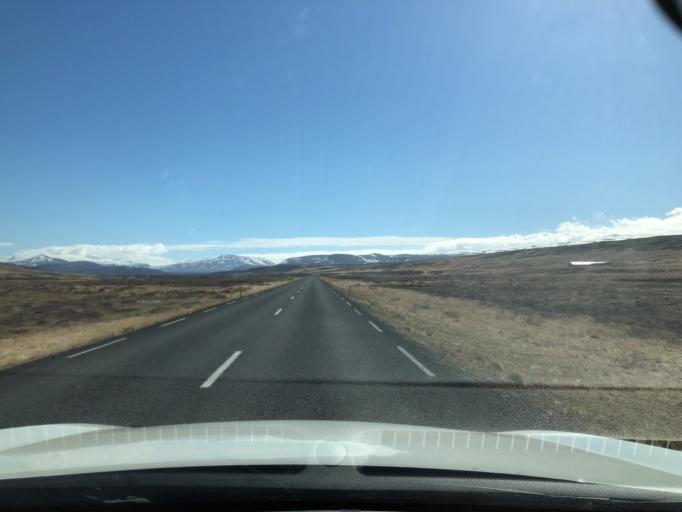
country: IS
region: South
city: Hveragerdi
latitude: 64.7021
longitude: -21.1060
